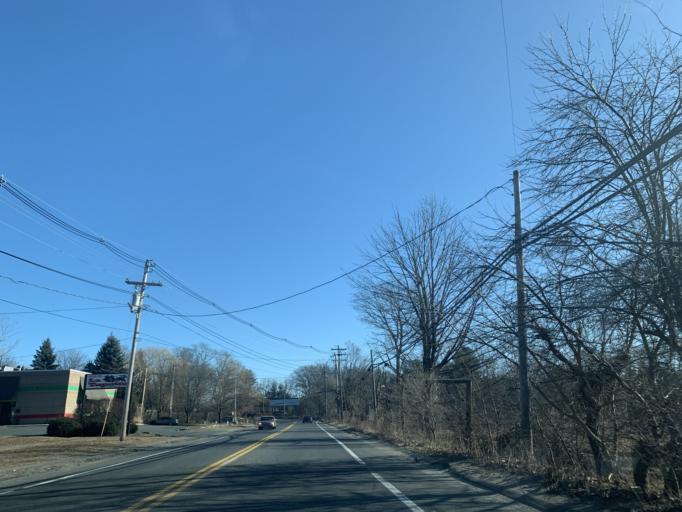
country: US
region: Massachusetts
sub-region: Middlesex County
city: Marlborough
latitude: 42.3488
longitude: -71.5165
